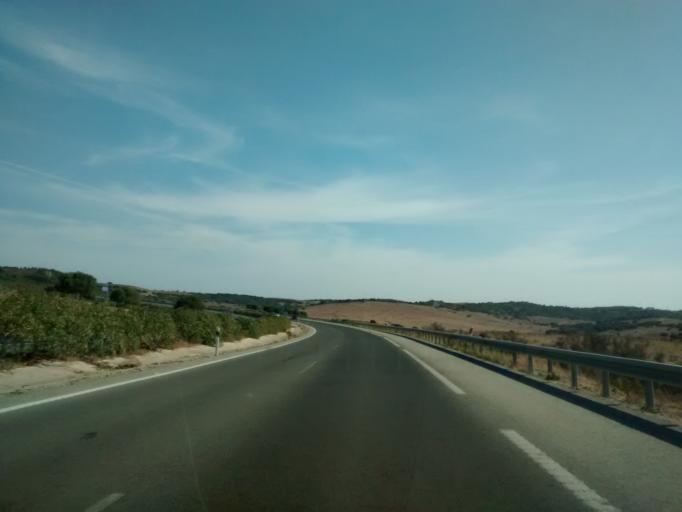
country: ES
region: Andalusia
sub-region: Provincia de Cadiz
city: Conil de la Frontera
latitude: 36.3330
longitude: -6.0505
